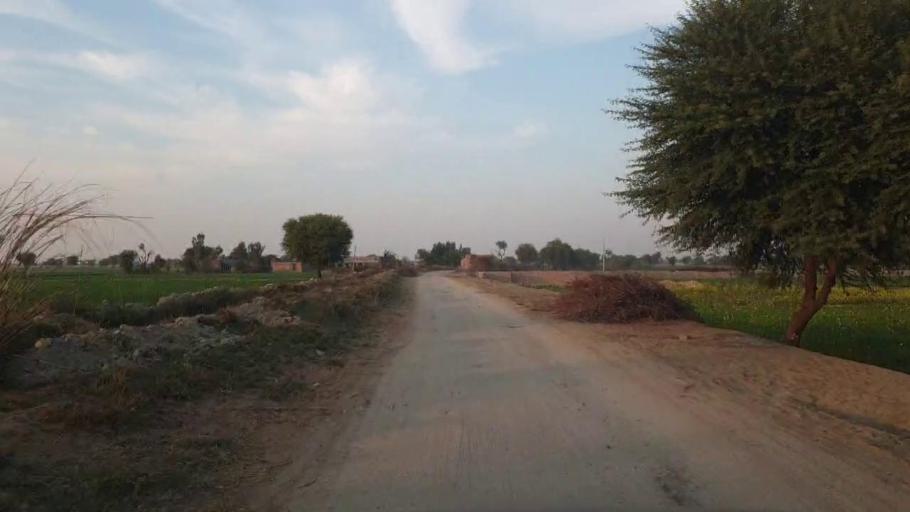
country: PK
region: Sindh
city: Shahpur Chakar
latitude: 26.1929
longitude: 68.6174
